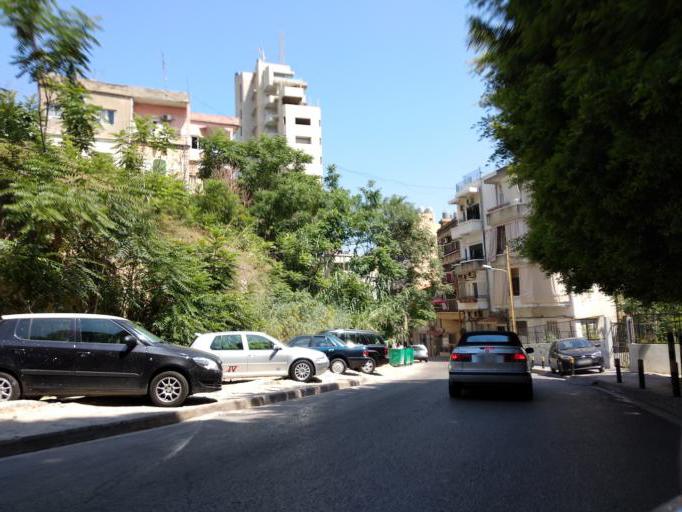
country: LB
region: Mont-Liban
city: Jdaidet el Matn
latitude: 33.8939
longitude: 35.5323
